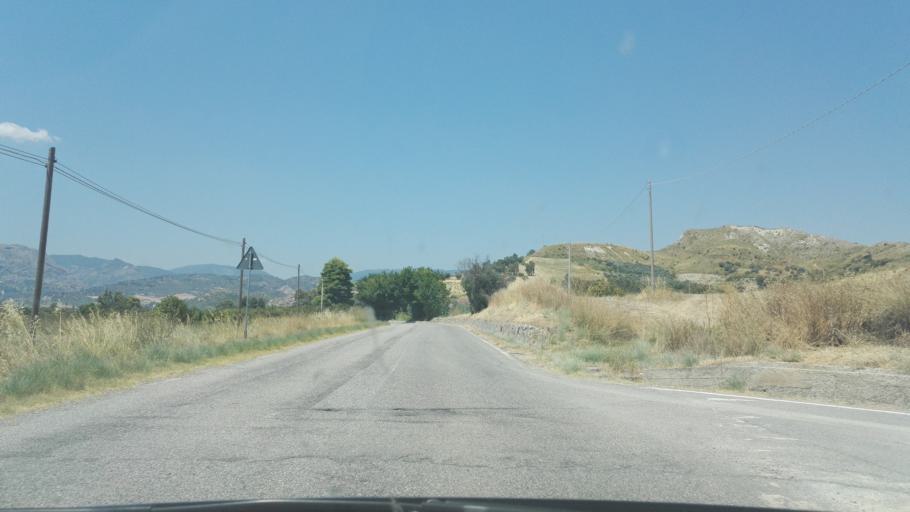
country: IT
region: Calabria
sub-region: Provincia di Reggio Calabria
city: Monasterace
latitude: 38.4471
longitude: 16.5343
